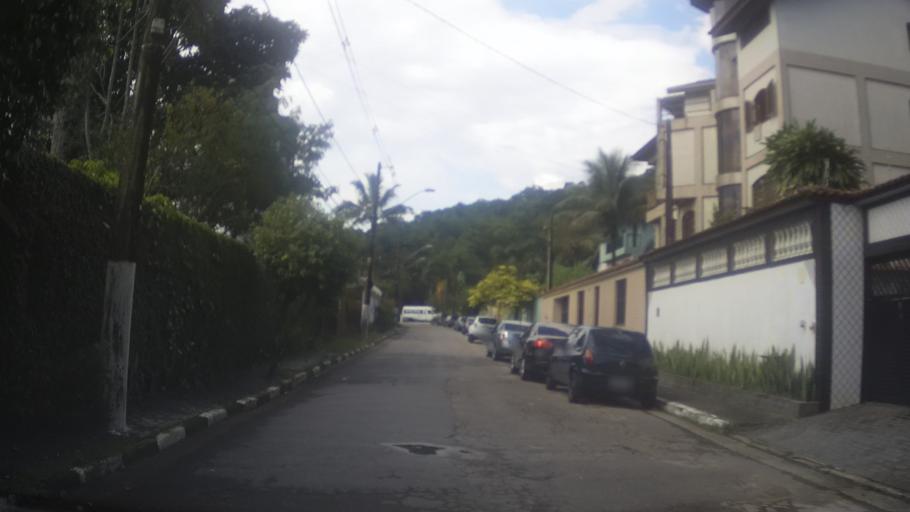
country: BR
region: Sao Paulo
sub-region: Santos
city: Santos
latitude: -23.9510
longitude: -46.3558
